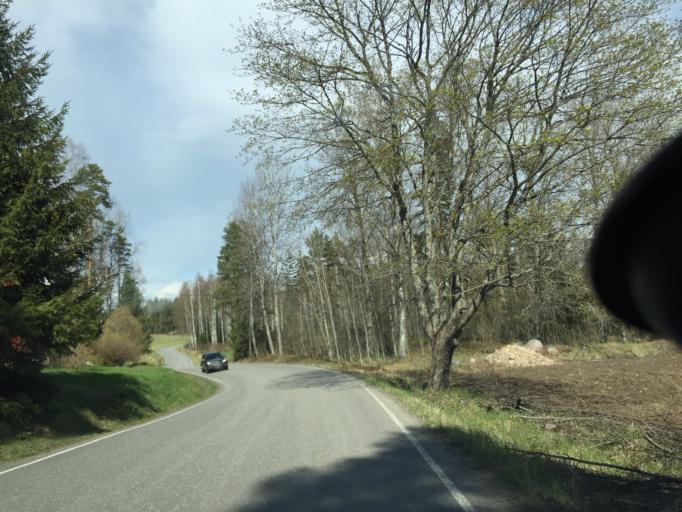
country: FI
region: Uusimaa
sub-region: Raaseporin
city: Hanko
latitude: 59.9447
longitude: 22.9528
